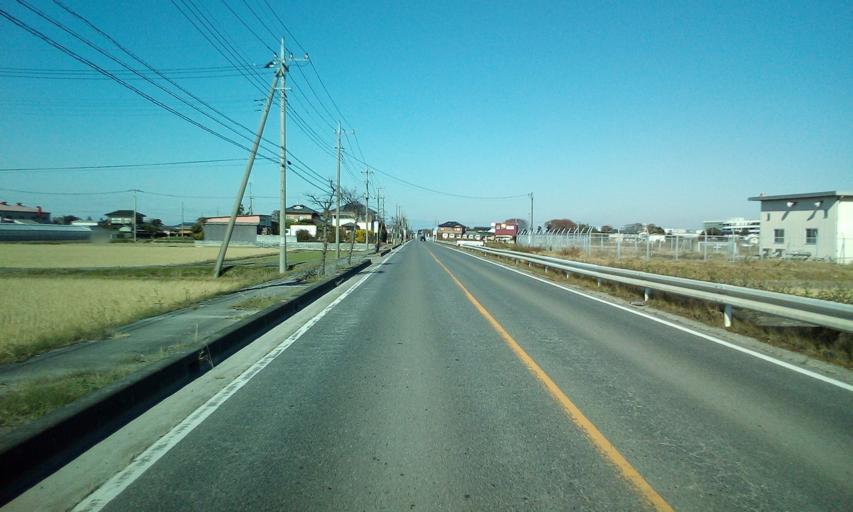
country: JP
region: Saitama
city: Kasukabe
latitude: 36.0251
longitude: 139.7891
